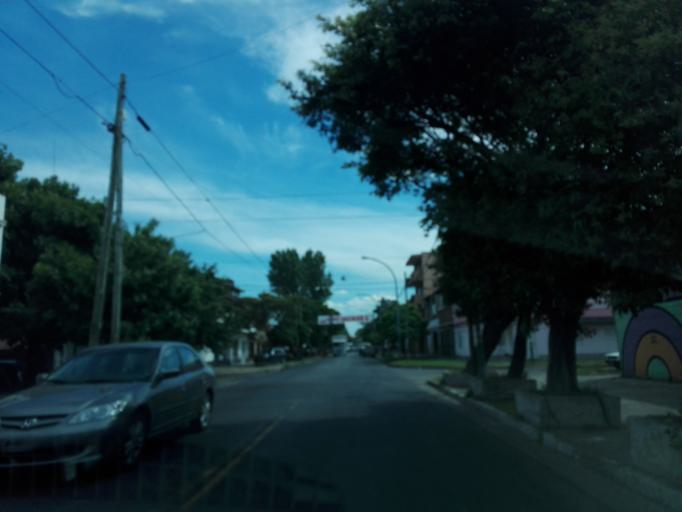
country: AR
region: Buenos Aires
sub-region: Partido de Lanus
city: Lanus
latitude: -34.7079
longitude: -58.3730
